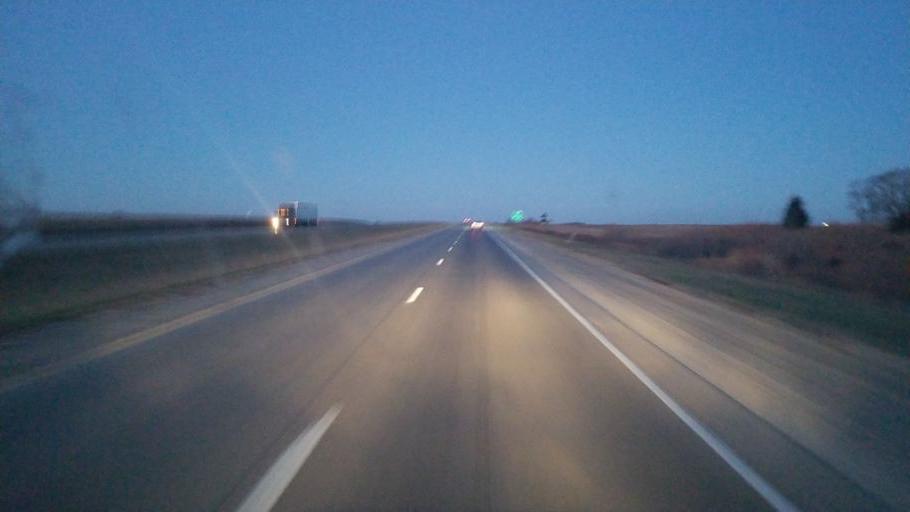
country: US
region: Iowa
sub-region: Henry County
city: New London
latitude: 40.9059
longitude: -91.3880
